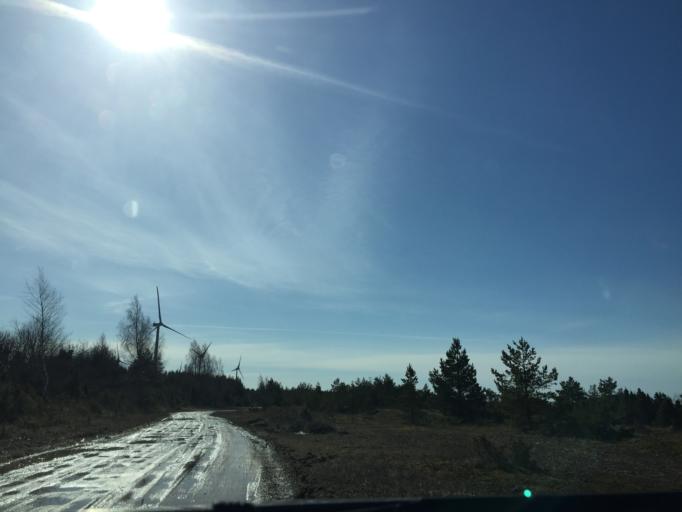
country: EE
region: Laeaene
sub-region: Haapsalu linn
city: Haapsalu
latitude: 58.6458
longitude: 23.5138
